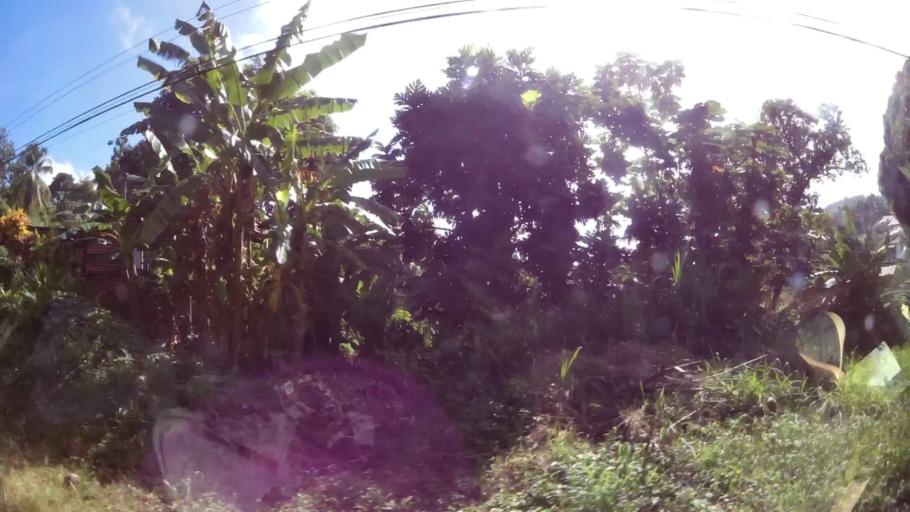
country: DM
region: Saint David
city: Castle Bruce
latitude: 15.4778
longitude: -61.2527
